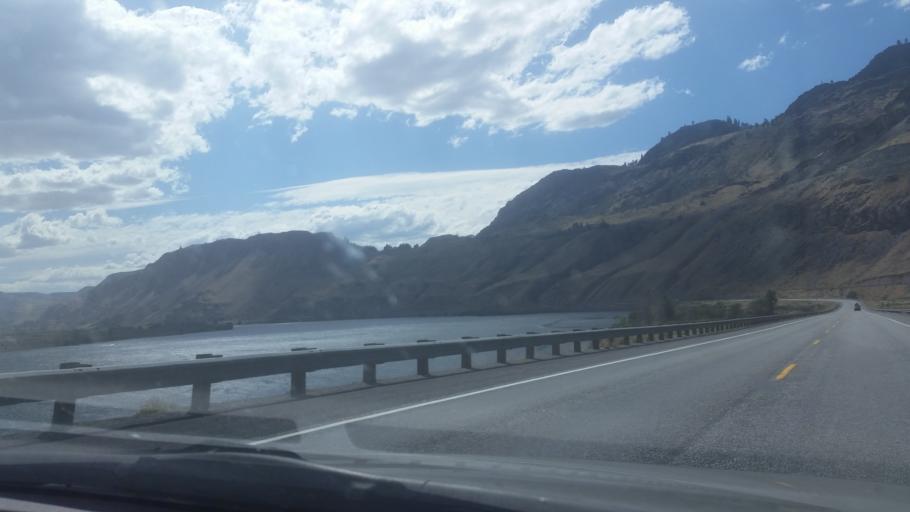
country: US
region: Washington
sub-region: Chelan County
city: Chelan
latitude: 47.8549
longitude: -119.9440
